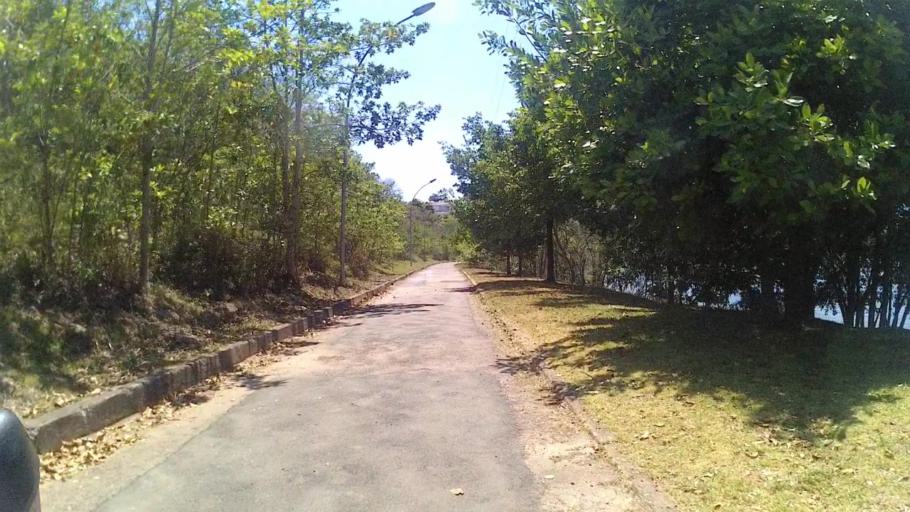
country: BR
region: Federal District
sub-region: Brasilia
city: Brasilia
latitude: -15.7289
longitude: -47.8855
